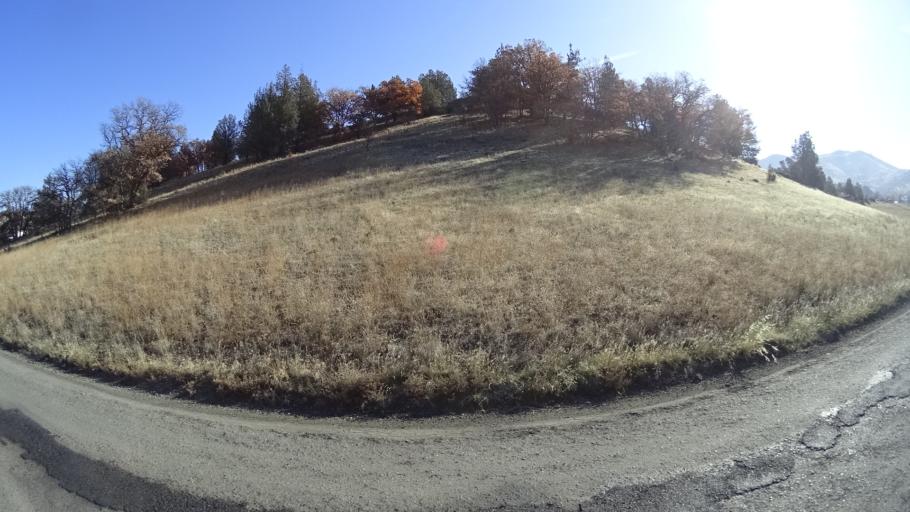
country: US
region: California
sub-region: Siskiyou County
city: Montague
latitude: 41.8864
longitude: -122.4267
